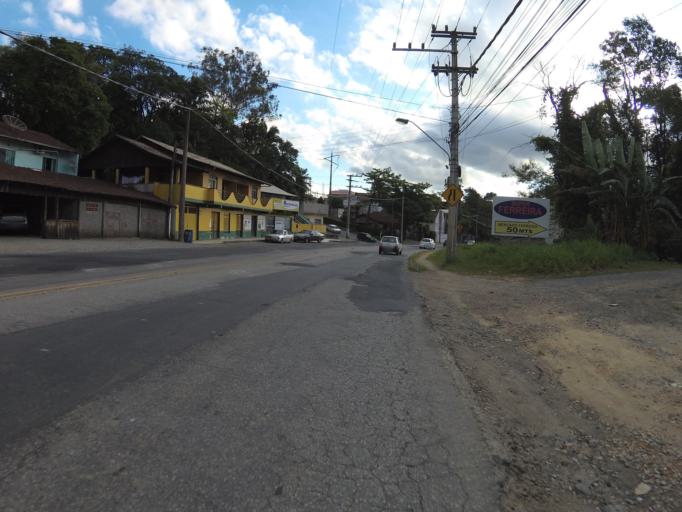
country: BR
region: Santa Catarina
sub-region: Blumenau
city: Blumenau
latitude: -26.8837
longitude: -49.1081
